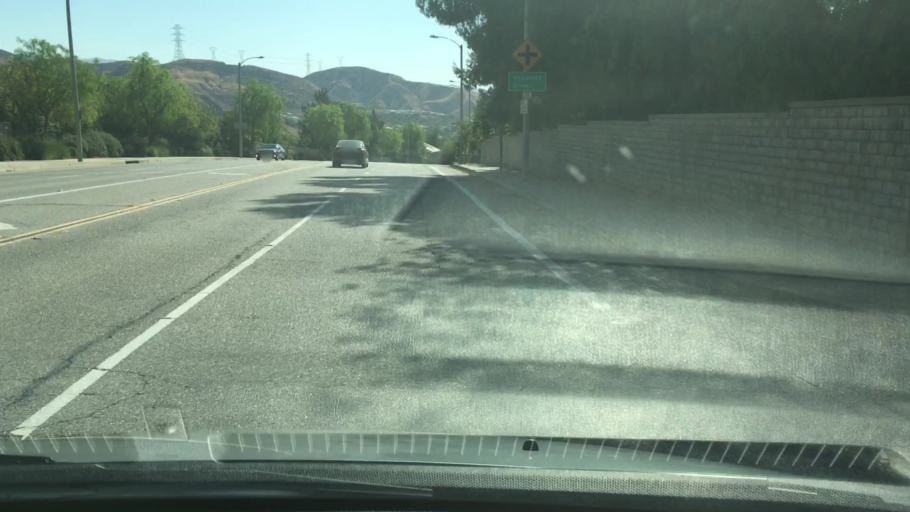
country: US
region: California
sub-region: Los Angeles County
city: Santa Clarita
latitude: 34.4594
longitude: -118.5189
